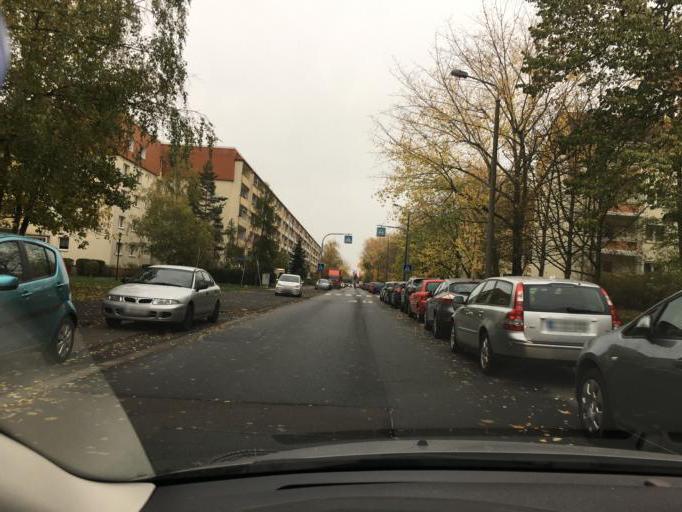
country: DE
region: Saxony
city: Leipzig
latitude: 51.3167
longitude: 12.3052
